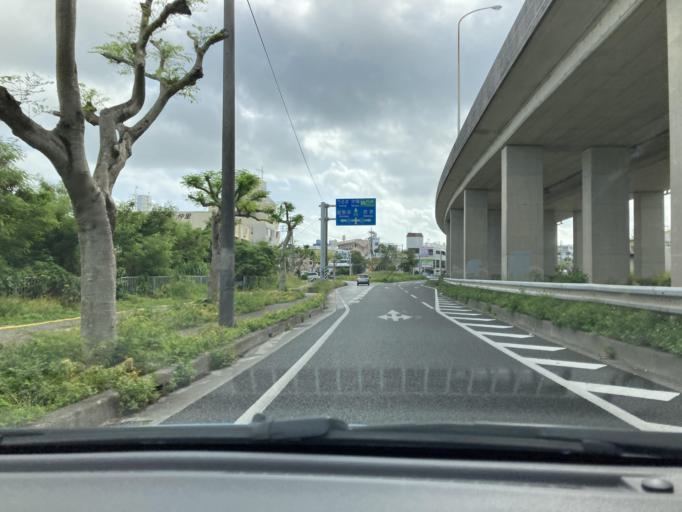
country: JP
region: Okinawa
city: Ginowan
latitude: 26.2542
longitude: 127.7375
